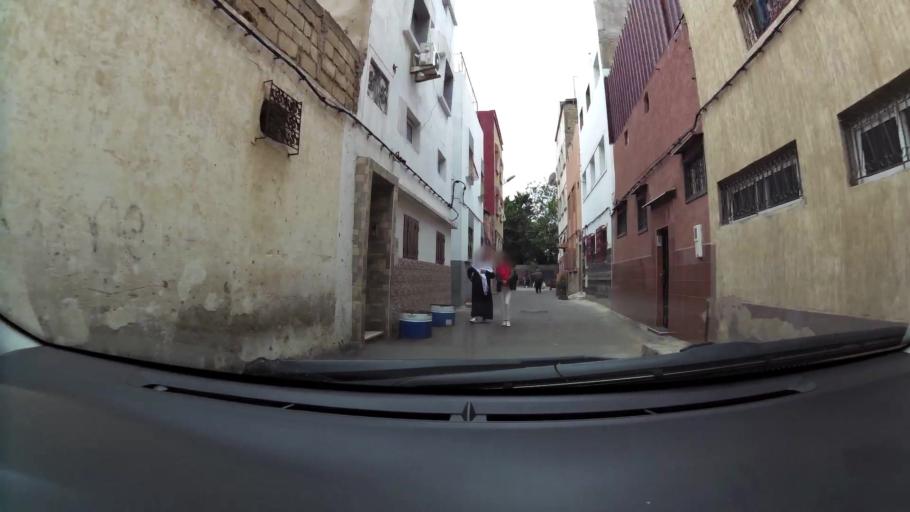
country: MA
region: Grand Casablanca
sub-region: Casablanca
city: Casablanca
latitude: 33.5678
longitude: -7.5679
